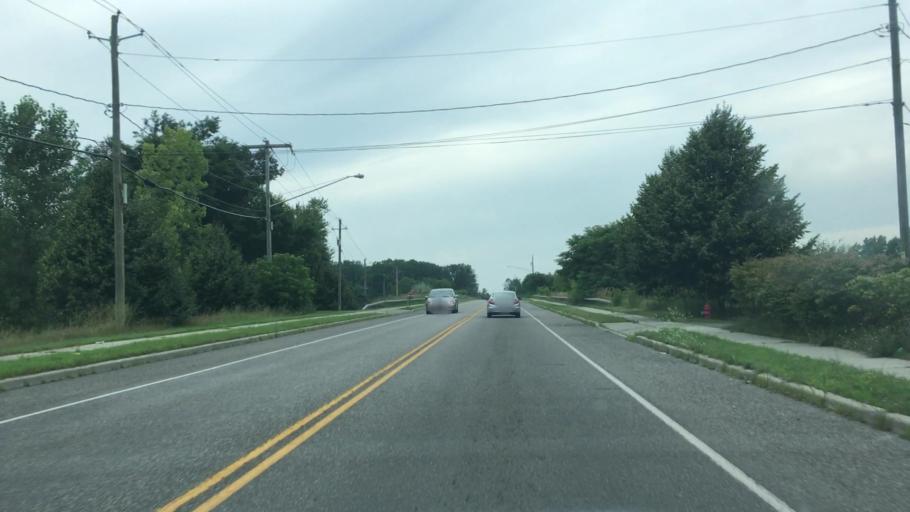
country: US
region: New York
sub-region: Clinton County
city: Plattsburgh West
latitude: 44.6871
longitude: -73.4875
